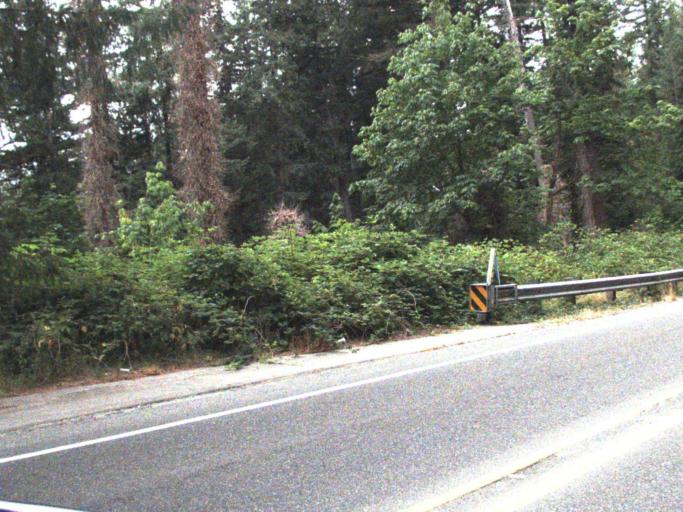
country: US
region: Washington
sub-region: King County
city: Snoqualmie
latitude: 47.5493
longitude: -121.8383
